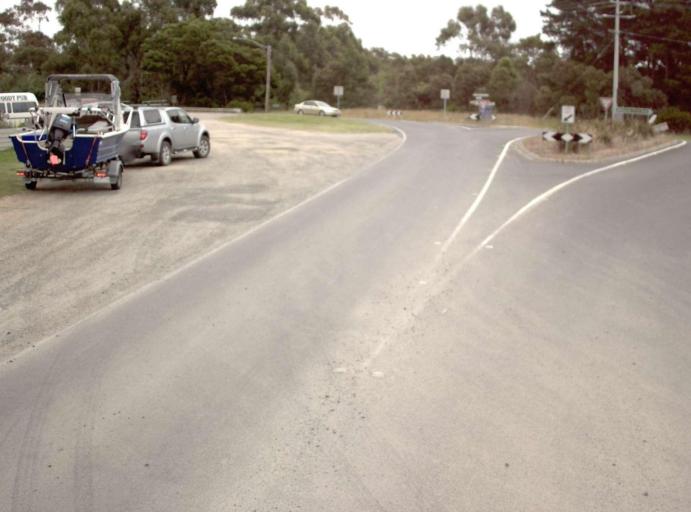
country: AU
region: Victoria
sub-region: Wellington
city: Sale
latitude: -38.5245
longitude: 146.8742
